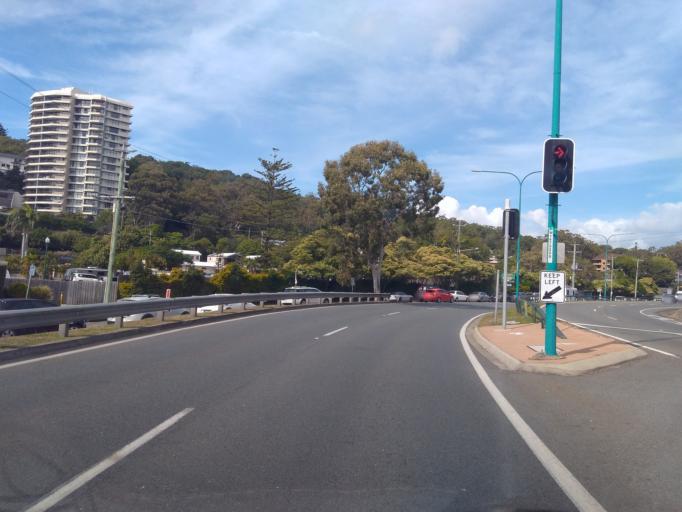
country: AU
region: Queensland
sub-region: Gold Coast
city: Palm Beach
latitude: -28.0911
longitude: 153.4538
